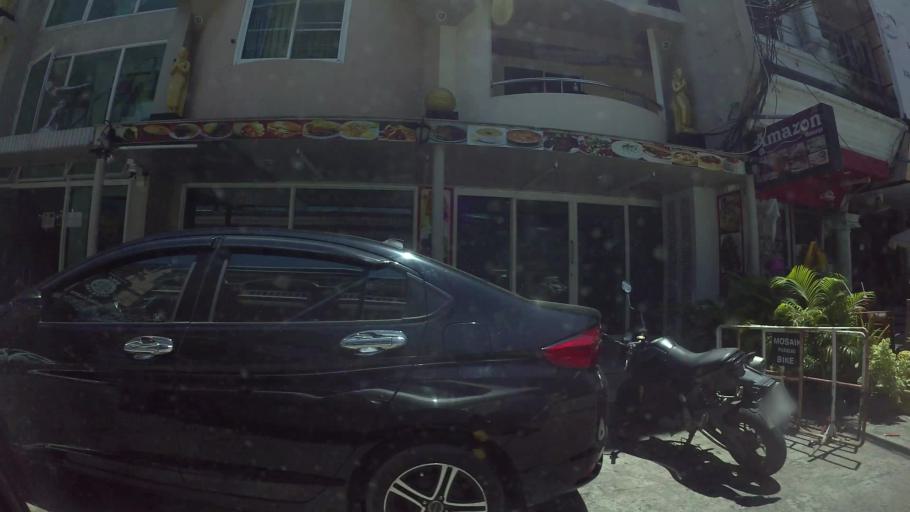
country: TH
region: Chon Buri
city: Phatthaya
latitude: 12.9232
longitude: 100.8787
